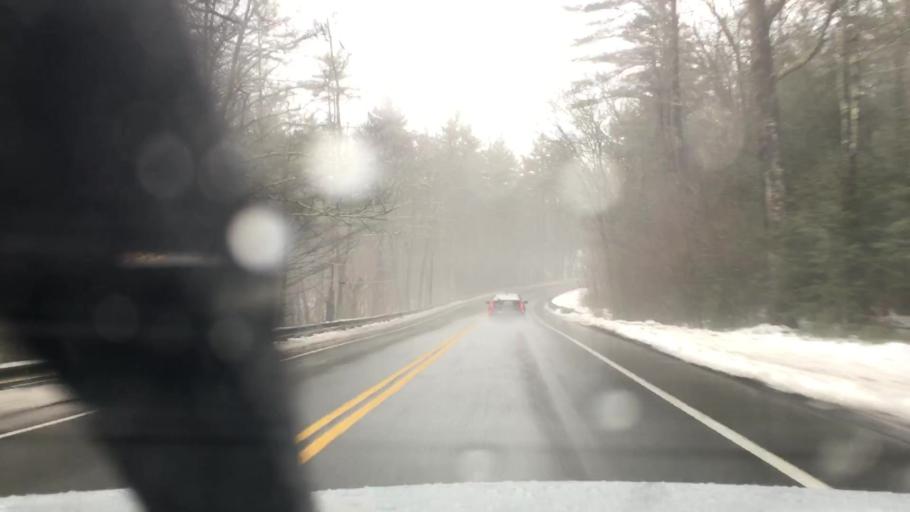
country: US
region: Massachusetts
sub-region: Franklin County
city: Orange
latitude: 42.5328
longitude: -72.3189
